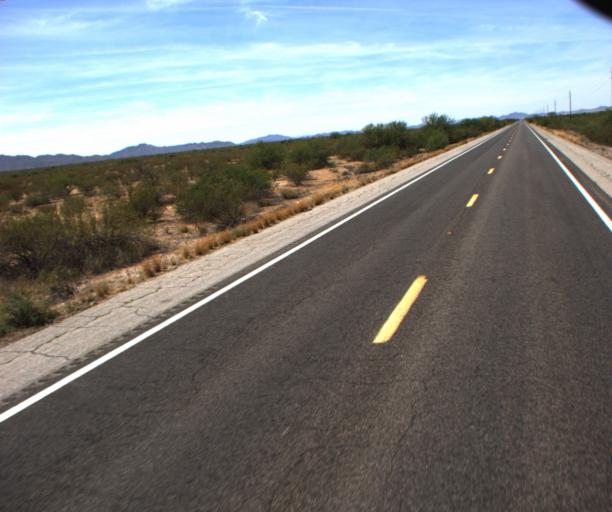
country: US
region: Arizona
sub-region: La Paz County
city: Salome
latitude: 33.8581
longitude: -113.4284
